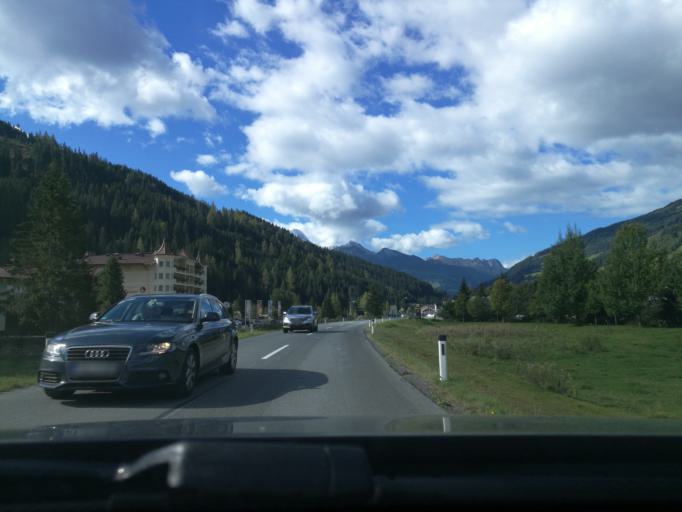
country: AT
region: Tyrol
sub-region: Politischer Bezirk Schwaz
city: Gerlos
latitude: 47.2299
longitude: 12.0519
